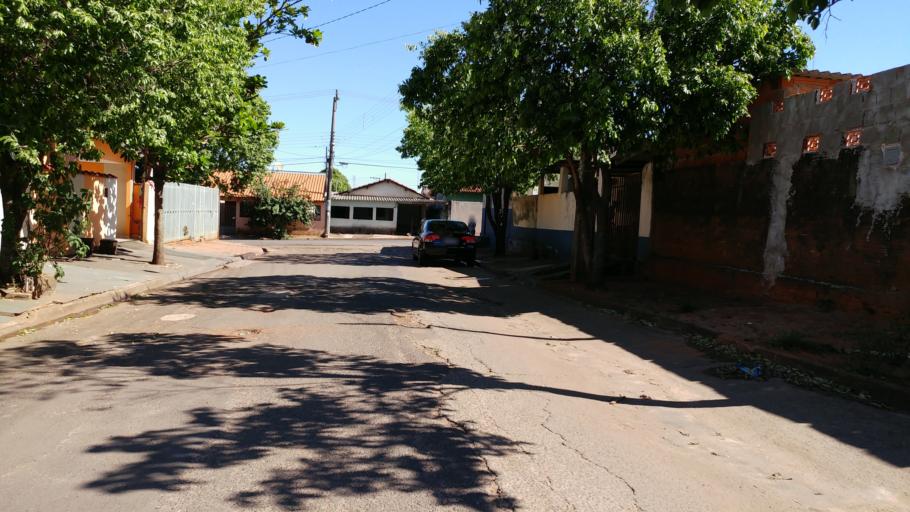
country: BR
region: Sao Paulo
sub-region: Paraguacu Paulista
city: Paraguacu Paulista
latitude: -22.4387
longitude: -50.5817
